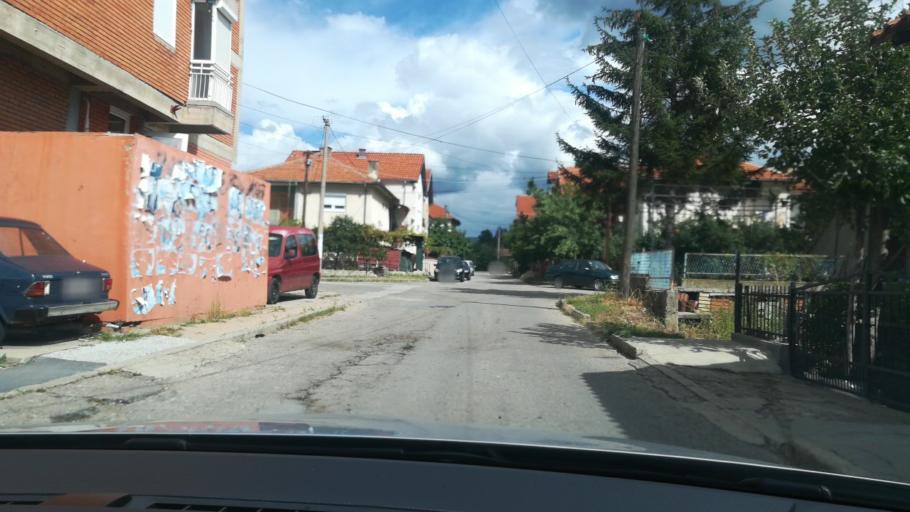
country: MK
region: Delcevo
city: Delcevo
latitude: 41.9631
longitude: 22.7789
